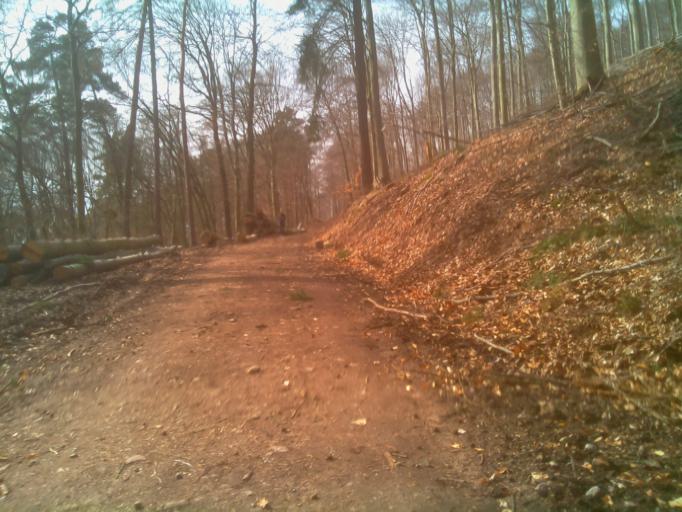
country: DE
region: Baden-Wuerttemberg
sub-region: Karlsruhe Region
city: Dossenheim
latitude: 49.4424
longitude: 8.6974
